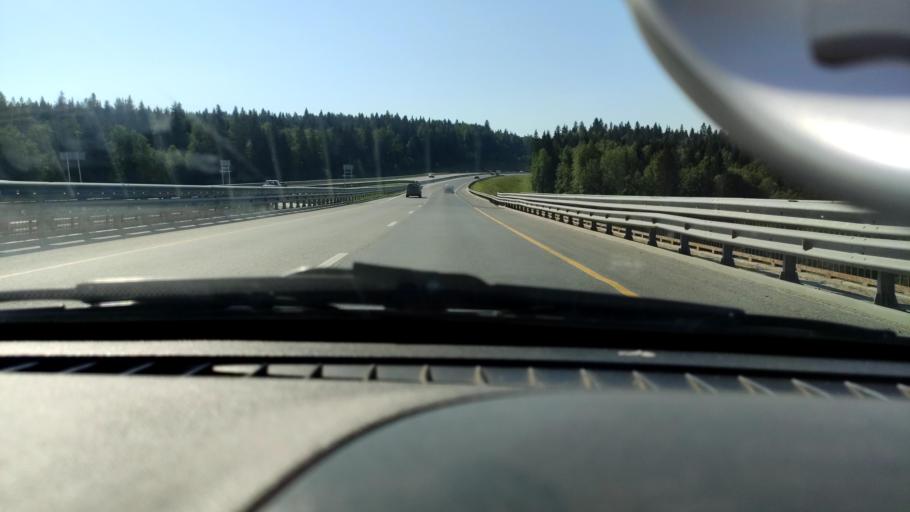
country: RU
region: Perm
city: Ferma
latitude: 57.9788
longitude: 56.3952
